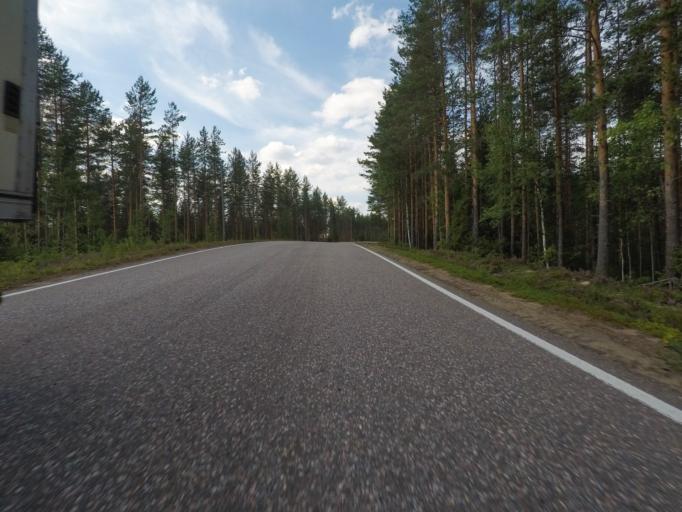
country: FI
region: Southern Savonia
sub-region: Savonlinna
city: Sulkava
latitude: 61.7393
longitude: 28.1988
